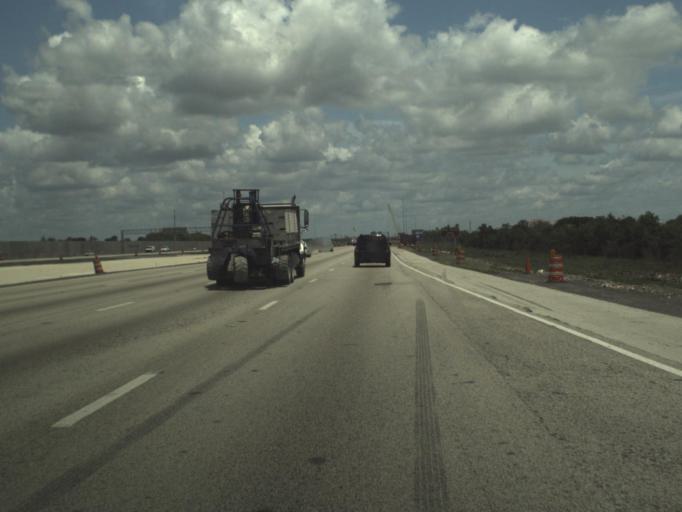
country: US
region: Florida
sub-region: Broward County
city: Sunshine Ranches
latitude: 26.0164
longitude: -80.3445
